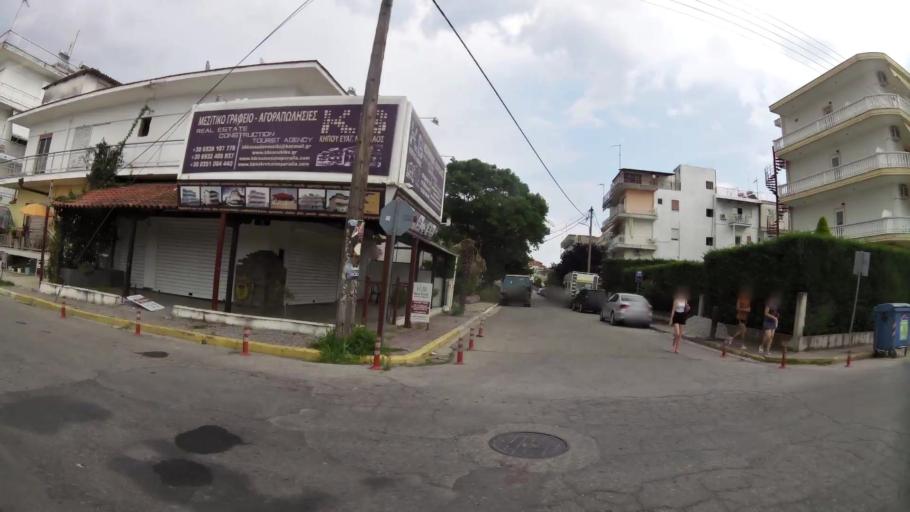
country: GR
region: Central Macedonia
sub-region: Nomos Pierias
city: Paralia
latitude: 40.2686
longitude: 22.5935
